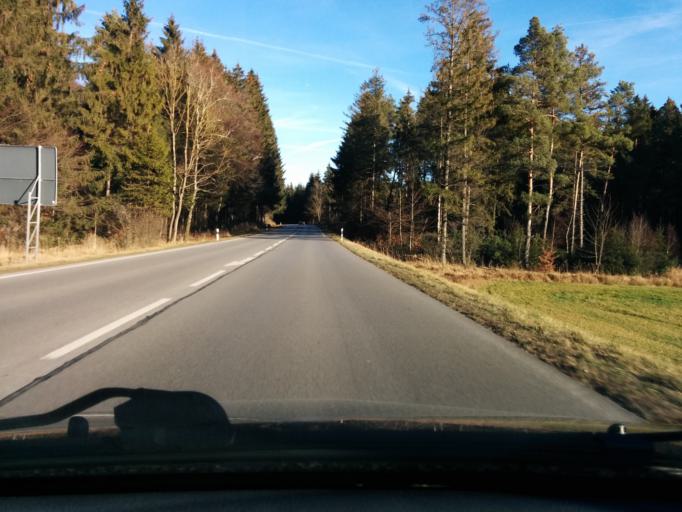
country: DE
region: Bavaria
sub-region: Upper Bavaria
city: Pahl
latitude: 47.9161
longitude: 11.2281
